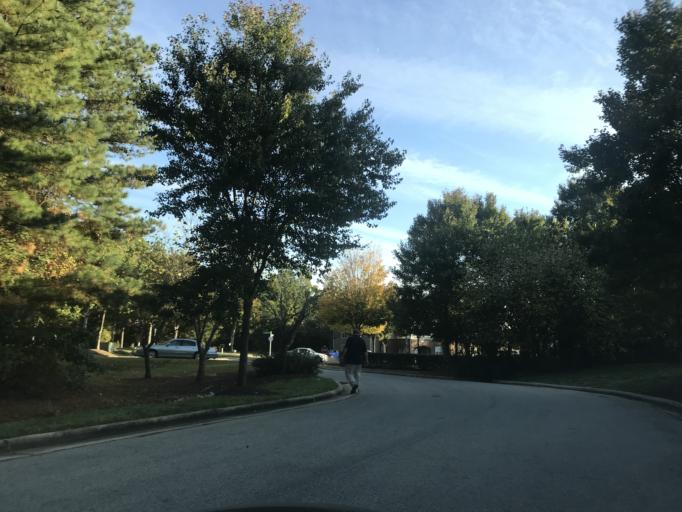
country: US
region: North Carolina
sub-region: Wake County
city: Wake Forest
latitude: 35.9092
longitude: -78.5965
